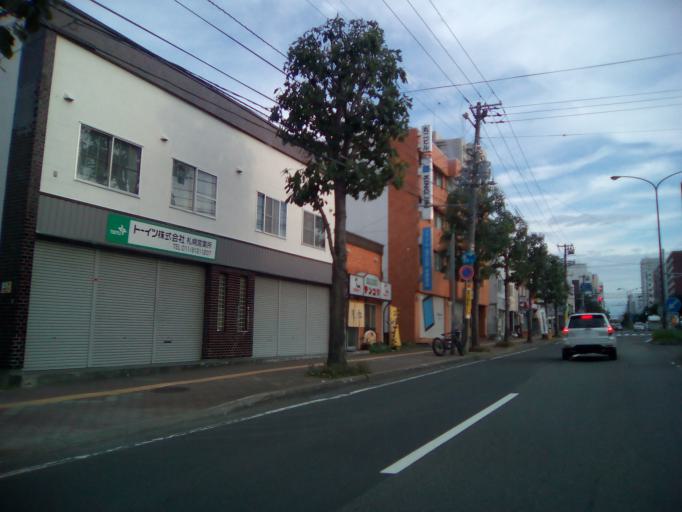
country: JP
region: Hokkaido
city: Sapporo
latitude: 43.0400
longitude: 141.3701
